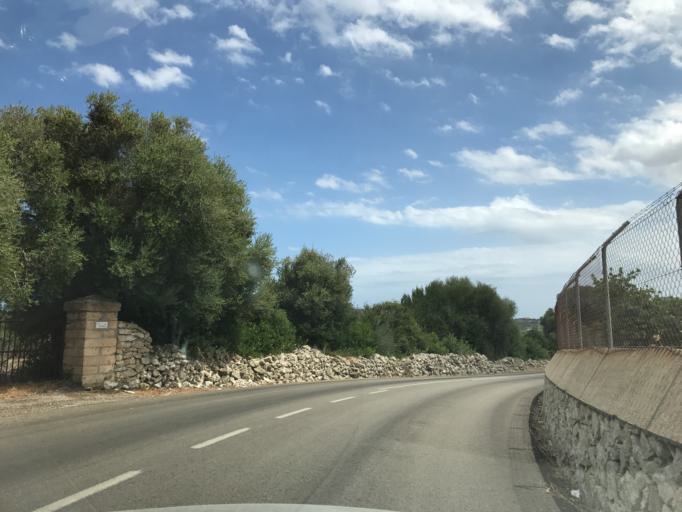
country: ES
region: Balearic Islands
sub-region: Illes Balears
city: Arta
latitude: 39.6587
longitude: 3.3417
